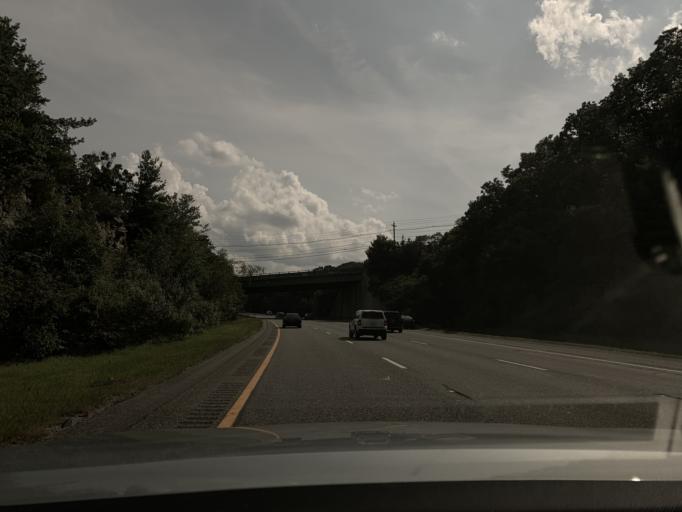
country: US
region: Rhode Island
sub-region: Providence County
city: Smithfield
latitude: 41.8976
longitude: -71.5233
